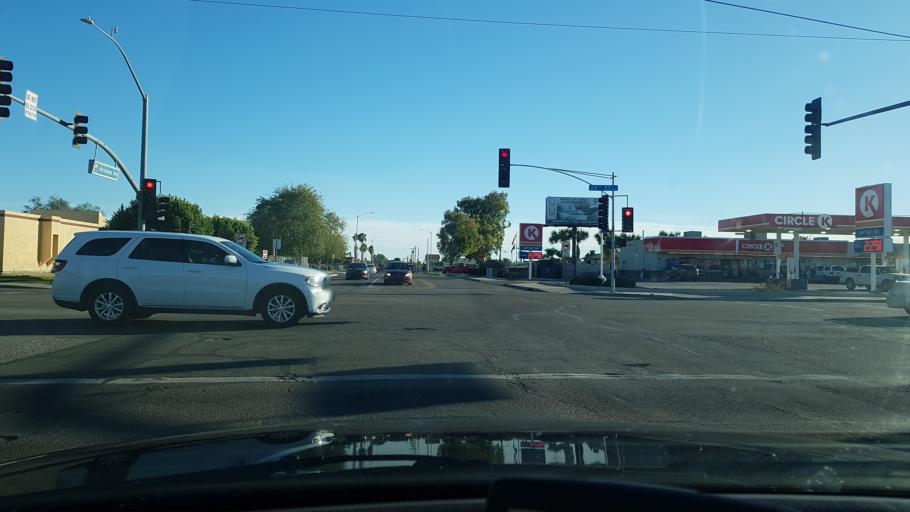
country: US
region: Arizona
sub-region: Yuma County
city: Yuma
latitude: 32.6842
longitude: -114.6160
